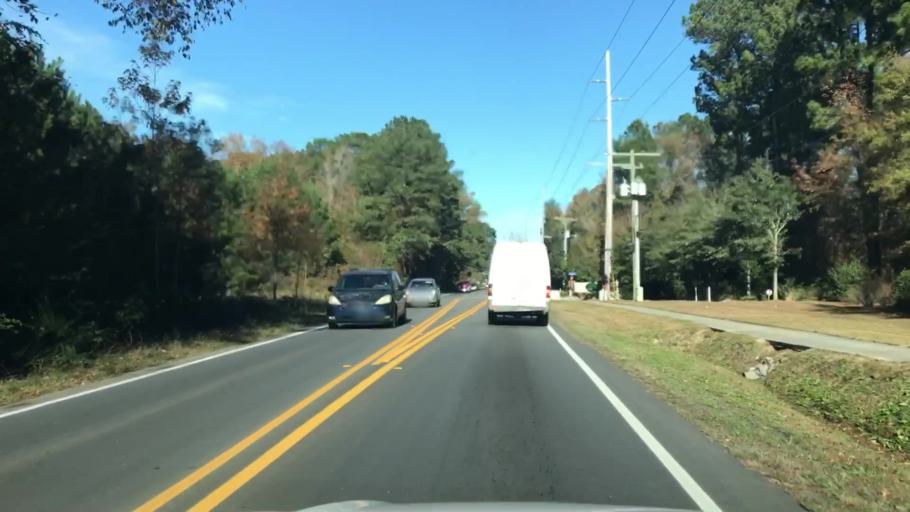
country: US
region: South Carolina
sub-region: Dorchester County
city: Summerville
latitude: 33.0013
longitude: -80.2317
